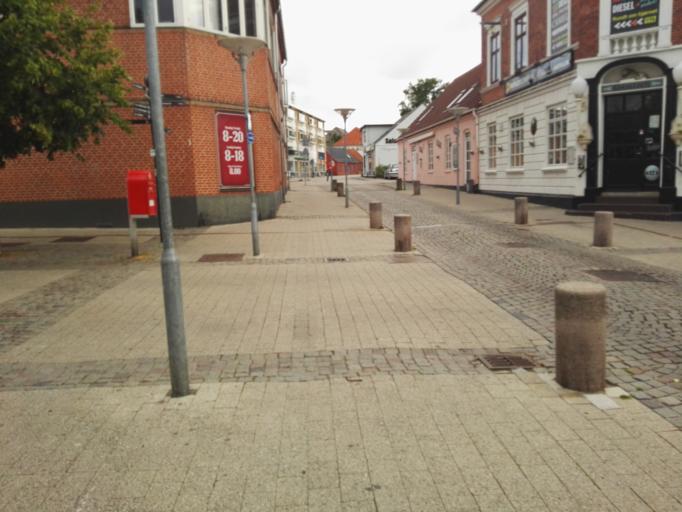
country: DK
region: Zealand
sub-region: Odsherred Kommune
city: Nykobing Sjaelland
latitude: 55.9226
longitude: 11.6706
